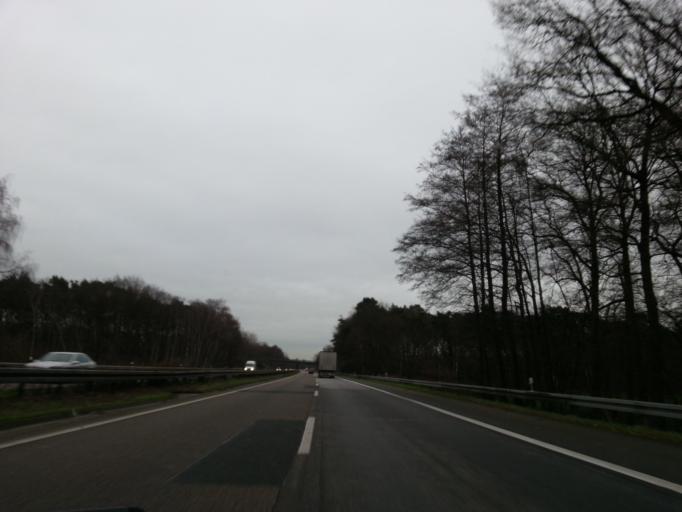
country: DE
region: North Rhine-Westphalia
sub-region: Regierungsbezirk Dusseldorf
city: Wesel
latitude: 51.7042
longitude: 6.6414
